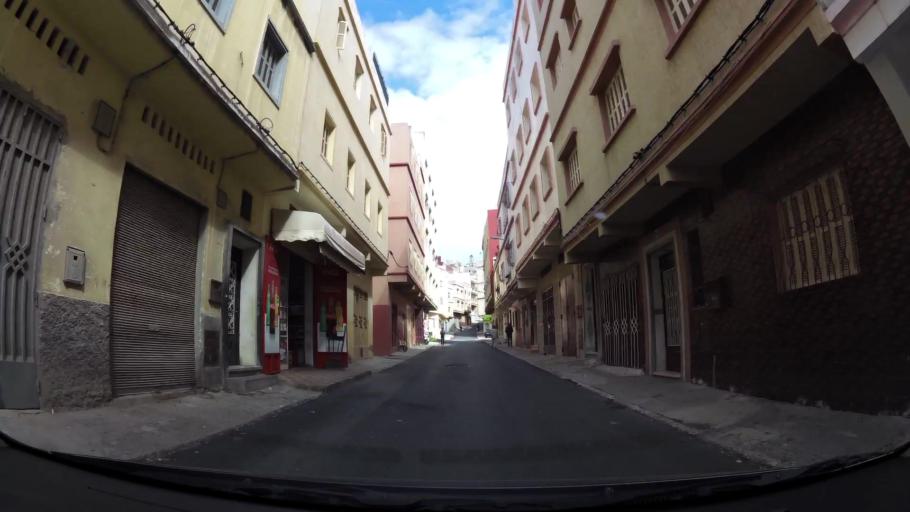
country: MA
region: Tanger-Tetouan
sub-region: Tanger-Assilah
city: Tangier
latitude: 35.7720
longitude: -5.8258
